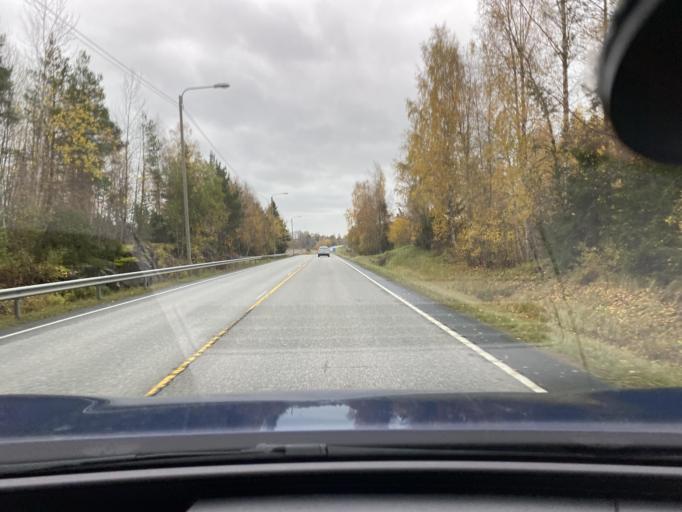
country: FI
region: Varsinais-Suomi
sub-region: Vakka-Suomi
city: Pyhaeranta
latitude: 60.9919
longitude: 21.5804
